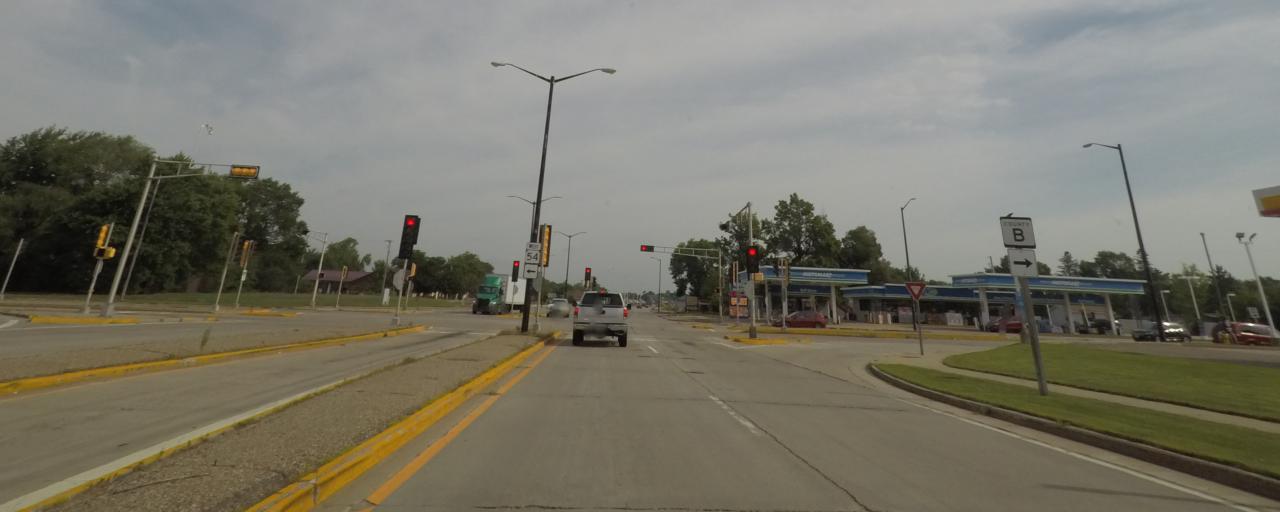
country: US
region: Wisconsin
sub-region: Portage County
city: Plover
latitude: 44.4532
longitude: -89.5441
